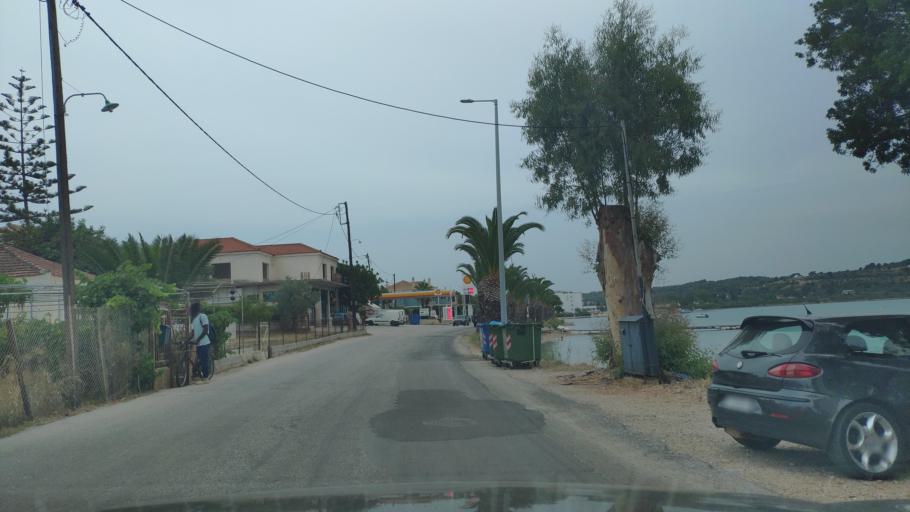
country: GR
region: Peloponnese
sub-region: Nomos Argolidos
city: Porto Cheli
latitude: 37.3230
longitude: 23.1563
